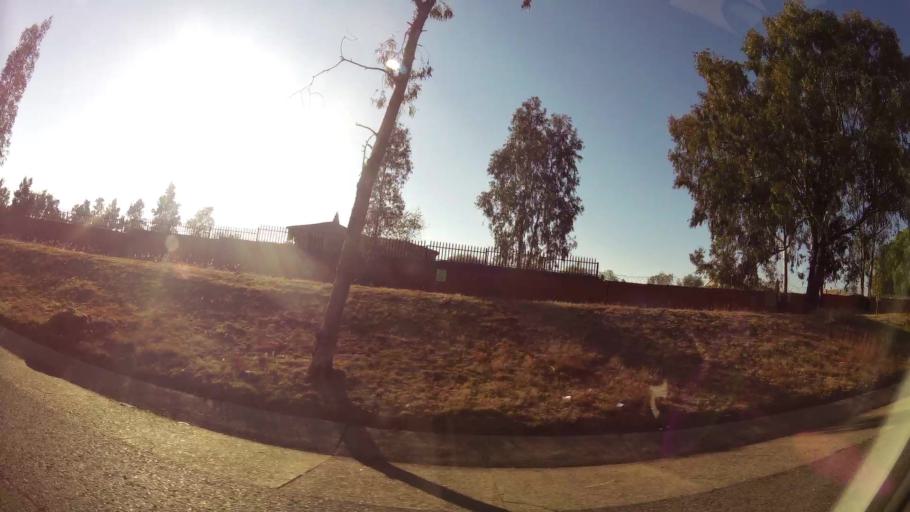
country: ZA
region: Gauteng
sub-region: Ekurhuleni Metropolitan Municipality
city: Germiston
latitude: -26.3493
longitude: 28.1022
